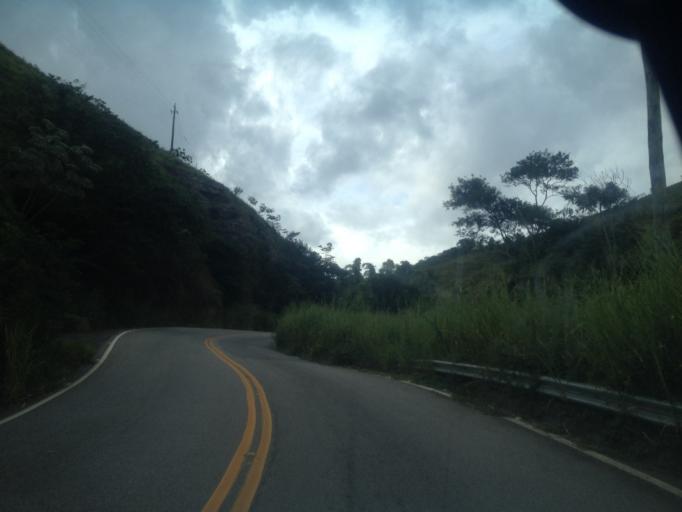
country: BR
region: Rio de Janeiro
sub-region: Quatis
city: Quatis
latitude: -22.3817
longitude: -44.2616
